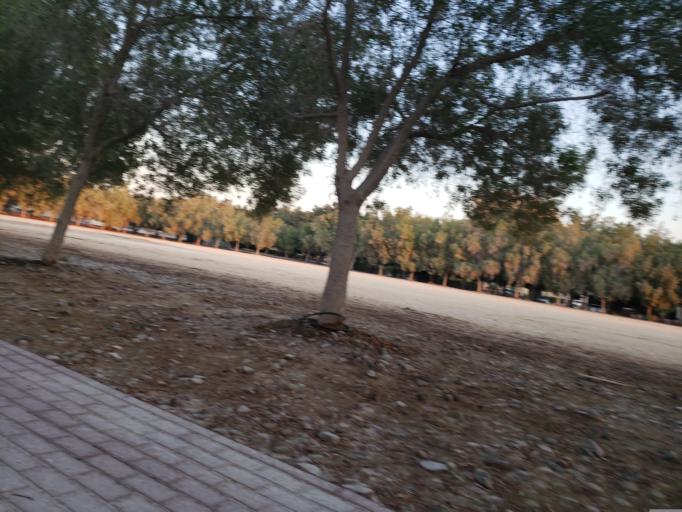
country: AE
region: Dubai
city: Dubai
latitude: 25.0090
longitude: 55.2493
